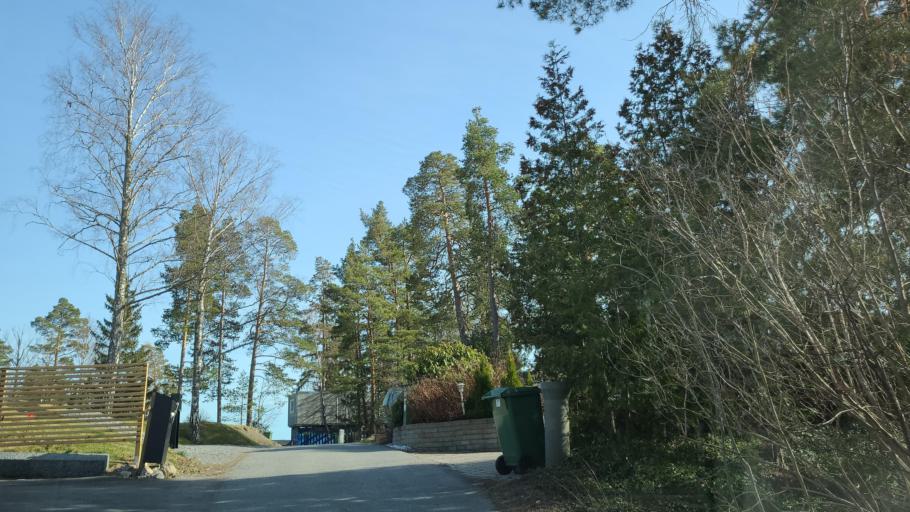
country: SE
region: Stockholm
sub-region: Ekero Kommun
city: Ekeroe
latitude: 59.2904
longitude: 17.7568
